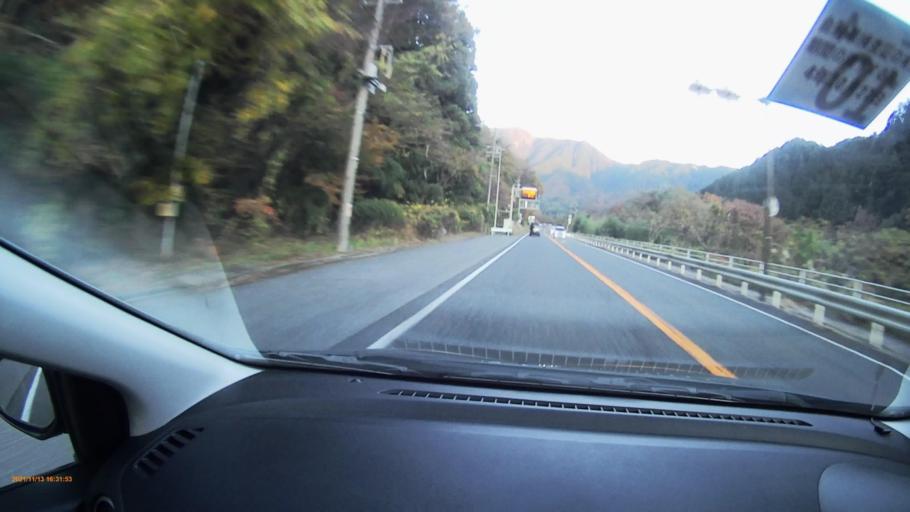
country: JP
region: Gifu
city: Nakatsugawa
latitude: 35.5890
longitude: 137.5818
